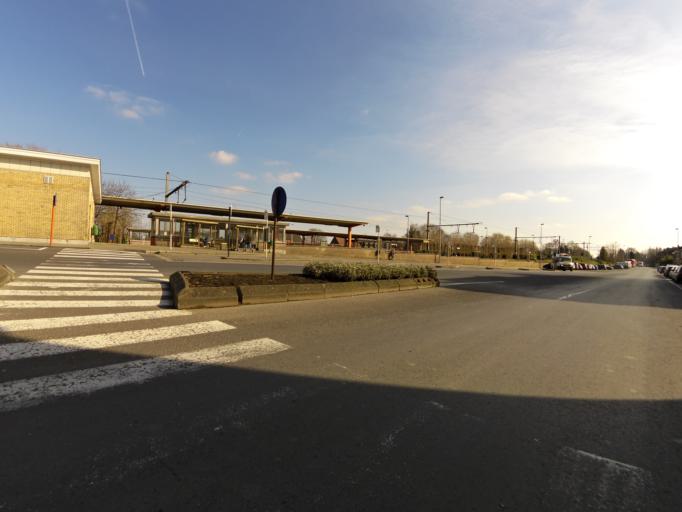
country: BE
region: Flanders
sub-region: Provincie West-Vlaanderen
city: Torhout
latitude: 51.0646
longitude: 3.1051
